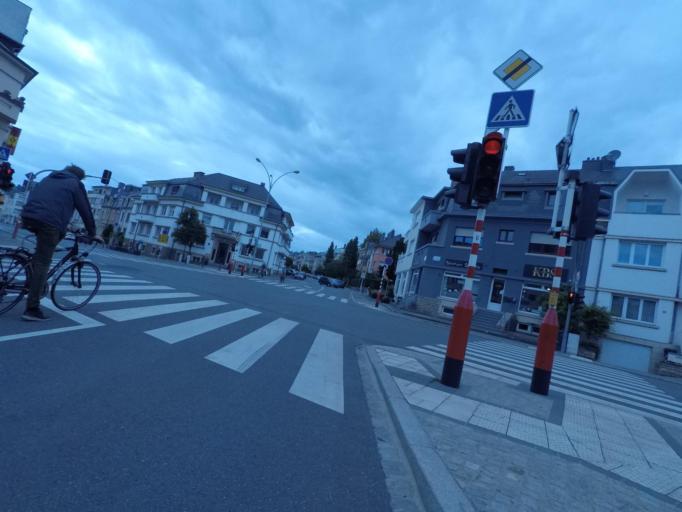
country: LU
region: Luxembourg
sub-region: Canton de Luxembourg
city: Luxembourg
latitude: 49.6080
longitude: 6.1123
